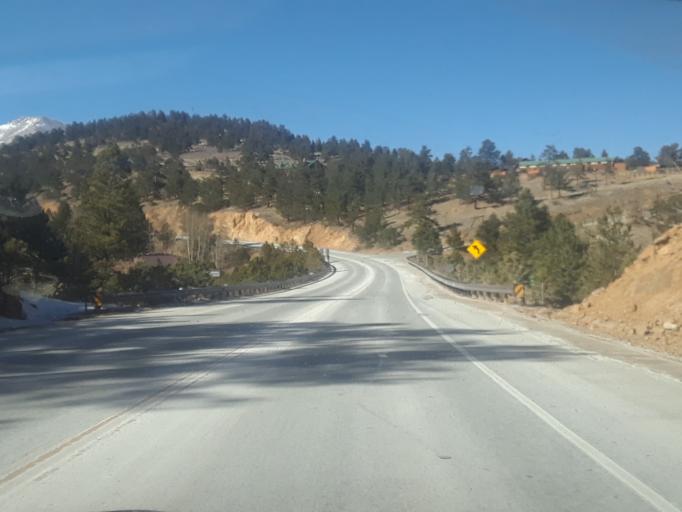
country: US
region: Colorado
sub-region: Larimer County
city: Estes Park
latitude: 40.1905
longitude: -105.5100
